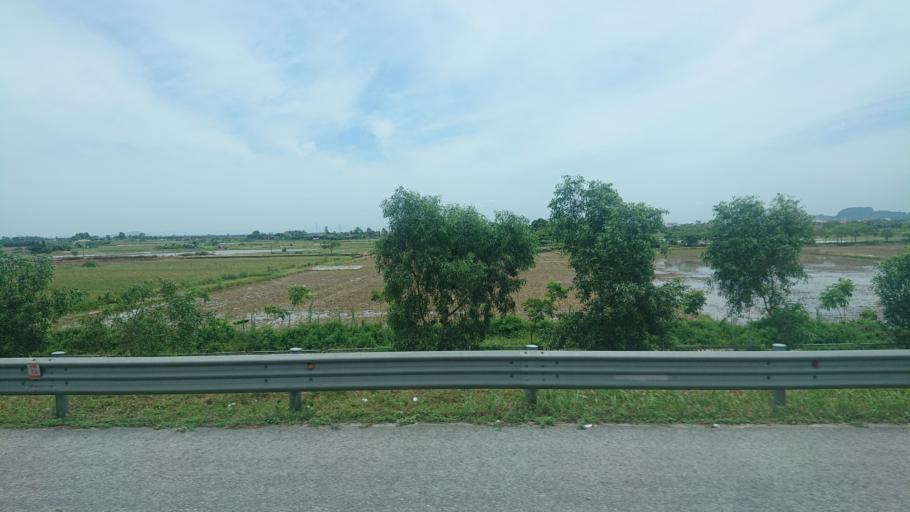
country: VN
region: Hai Phong
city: An Lao
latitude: 20.8054
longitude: 106.5193
